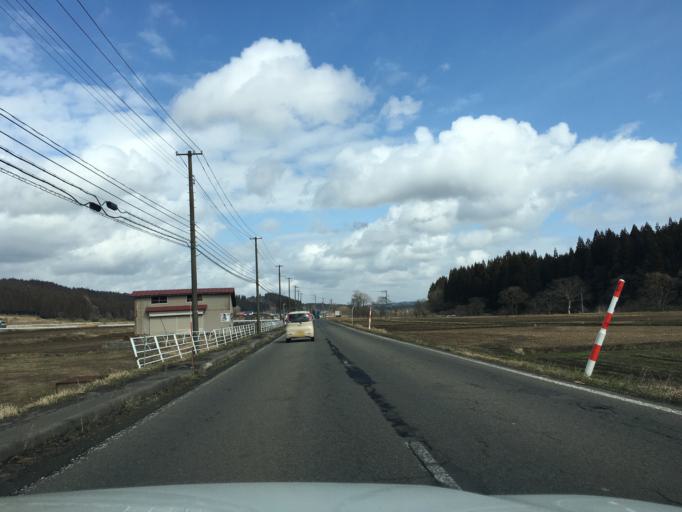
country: JP
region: Akita
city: Takanosu
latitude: 40.0360
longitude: 140.2765
